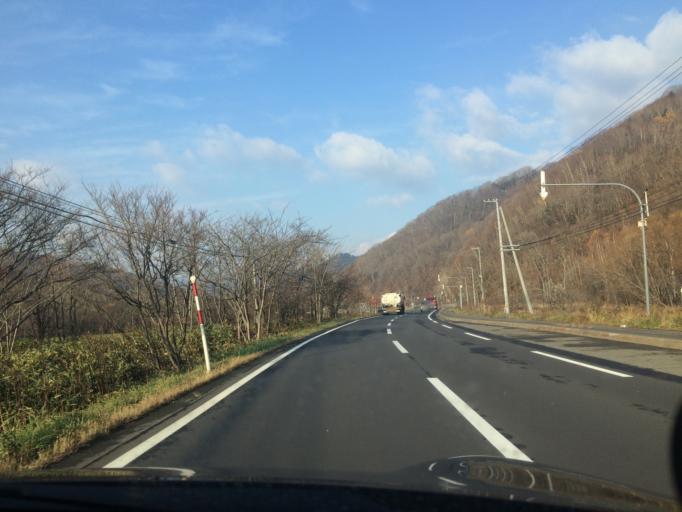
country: JP
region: Hokkaido
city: Shimo-furano
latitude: 42.8943
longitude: 142.5071
